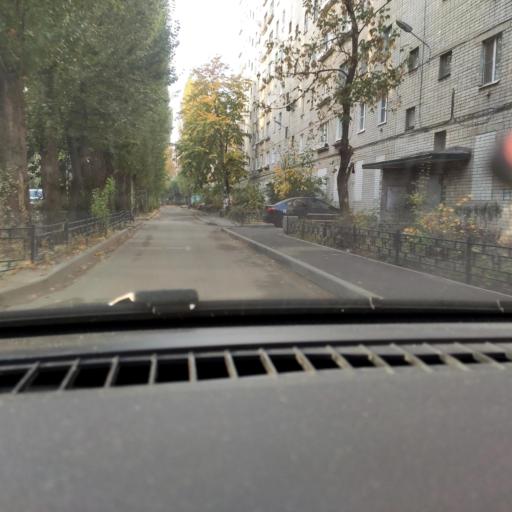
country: RU
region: Voronezj
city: Voronezh
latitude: 51.6963
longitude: 39.2589
